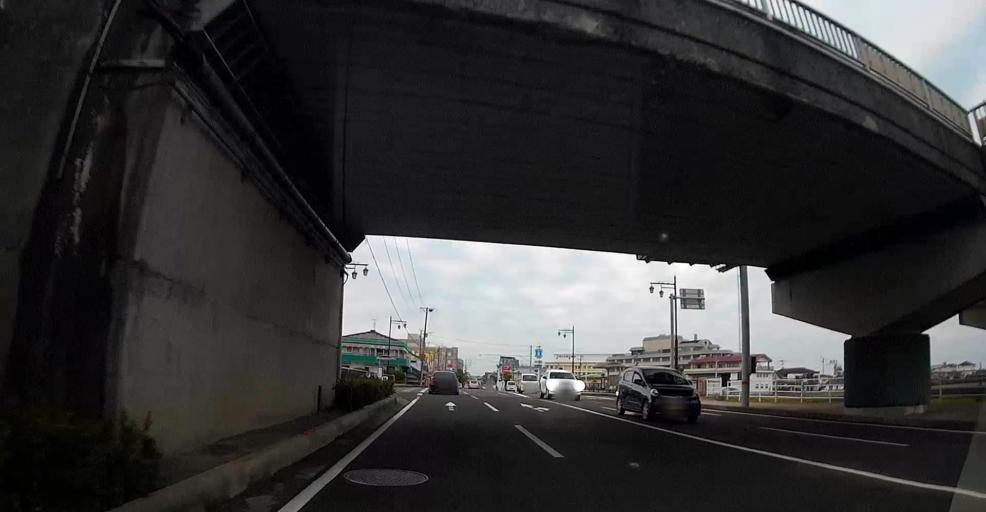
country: JP
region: Kumamoto
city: Hondo
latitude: 32.4471
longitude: 130.2008
